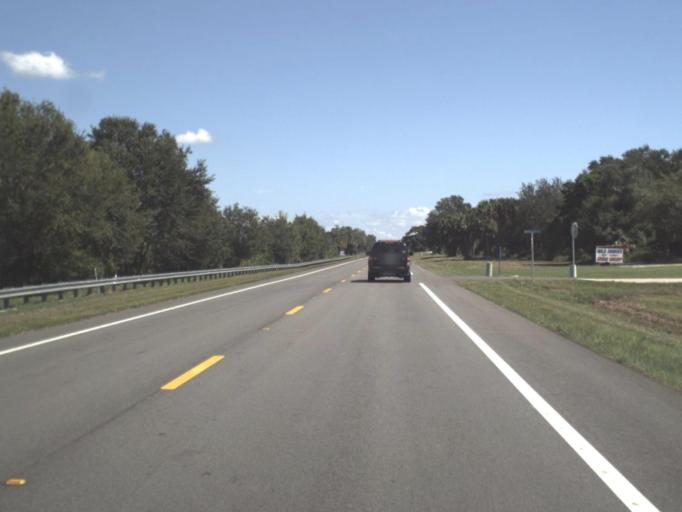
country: US
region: Florida
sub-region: Glades County
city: Moore Haven
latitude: 26.9942
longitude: -81.0811
